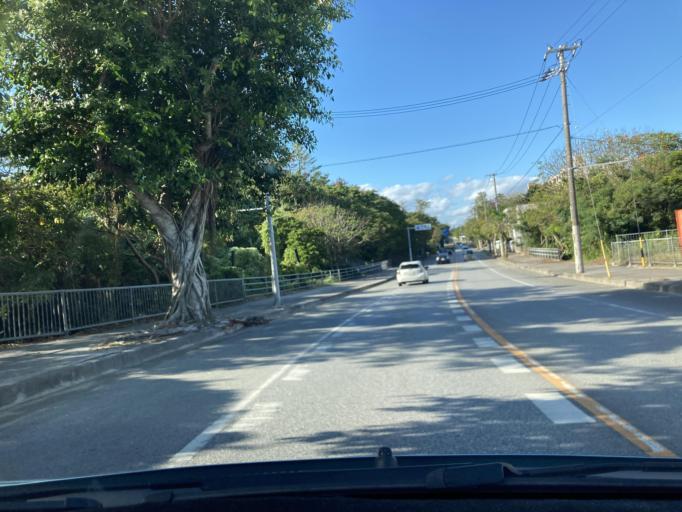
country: JP
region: Okinawa
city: Gushikawa
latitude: 26.3693
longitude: 127.8303
